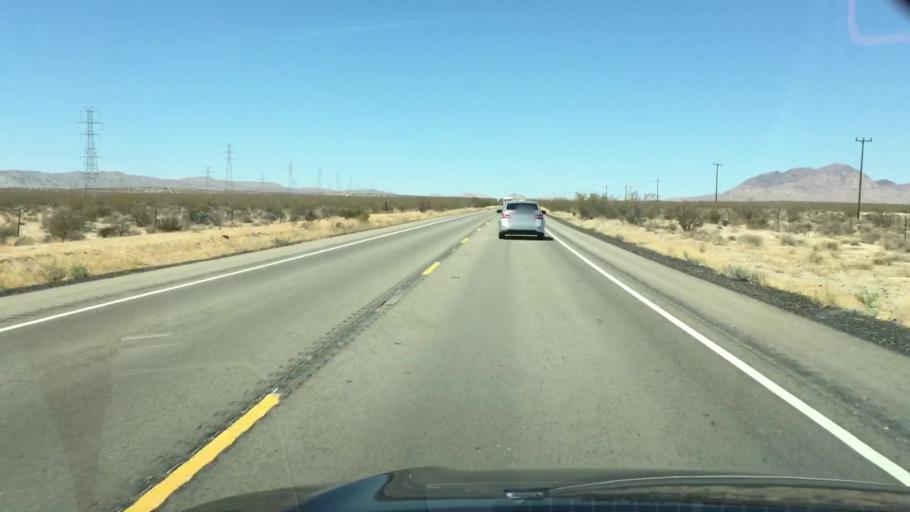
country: US
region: California
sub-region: Kern County
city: Boron
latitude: 35.2427
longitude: -117.6103
